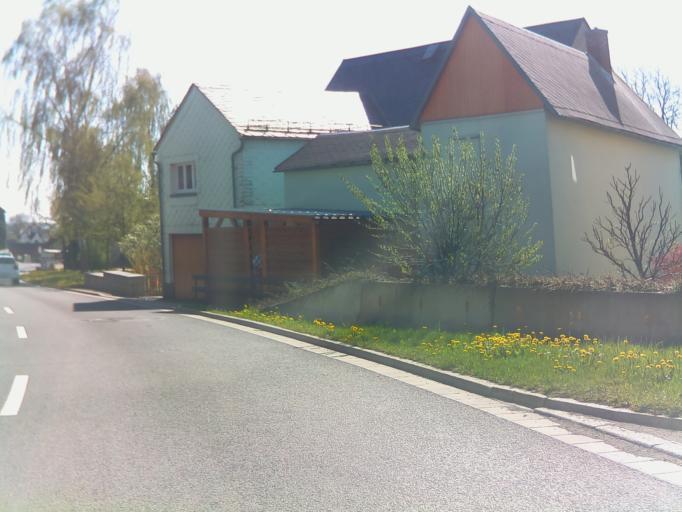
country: DE
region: Saxony
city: Muhltroff
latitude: 50.5322
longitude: 11.8927
